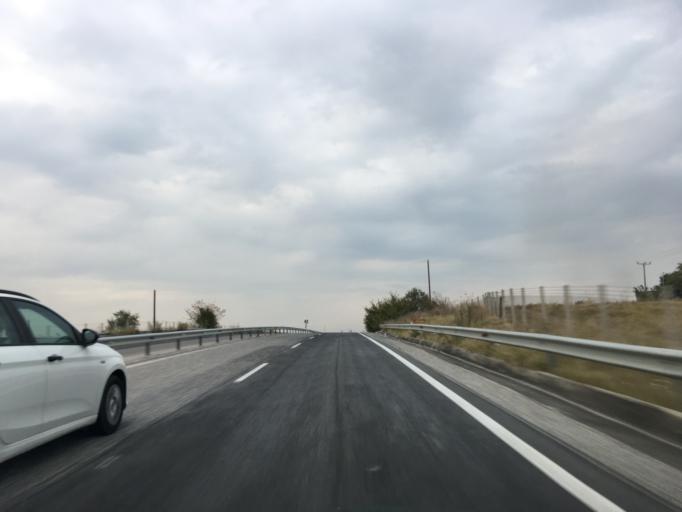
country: GR
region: Thessaly
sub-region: Nomos Larisis
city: Terpsithea
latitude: 39.6200
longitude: 22.2606
